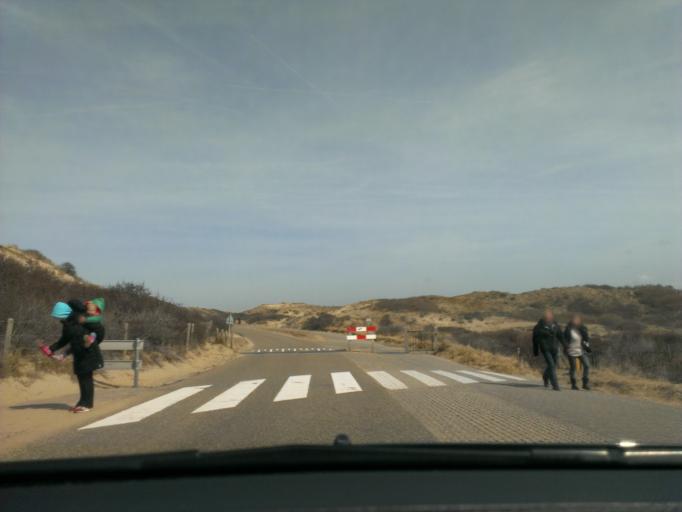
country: NL
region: North Holland
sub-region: Gemeente Zandvoort
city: Zandvoort
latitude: 52.4078
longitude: 4.5491
